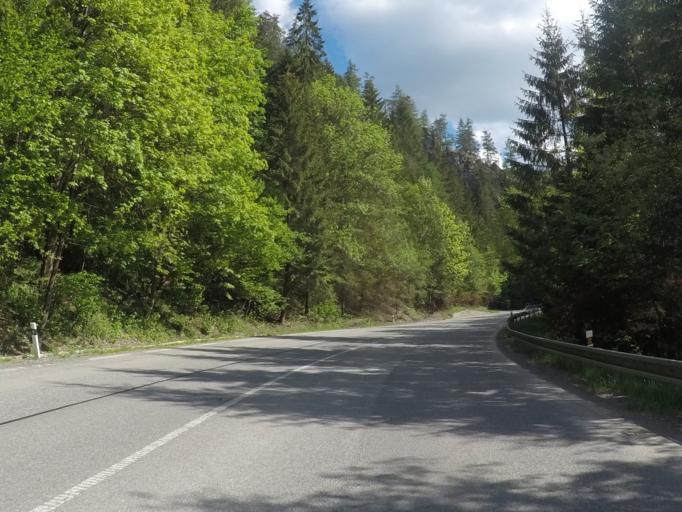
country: SK
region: Presovsky
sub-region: Okres Poprad
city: Poprad
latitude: 48.9342
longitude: 20.2859
